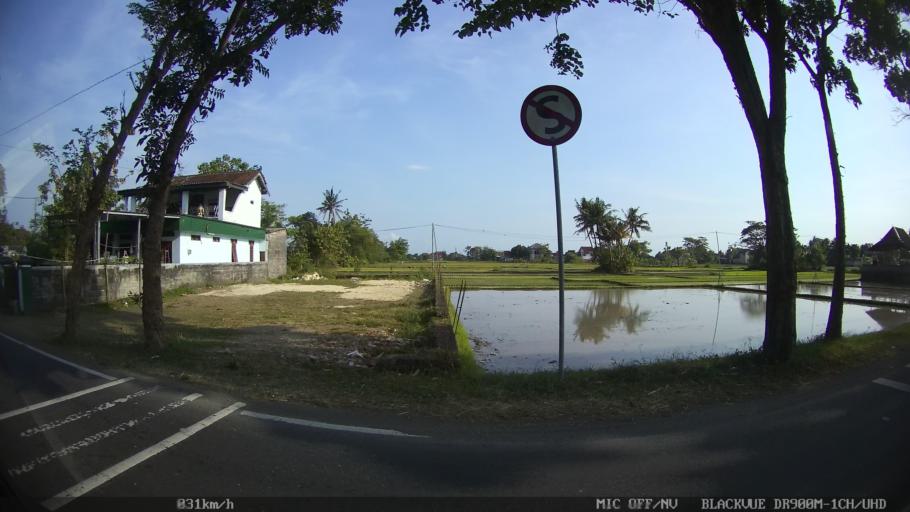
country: ID
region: Daerah Istimewa Yogyakarta
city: Bantul
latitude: -7.8783
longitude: 110.3287
